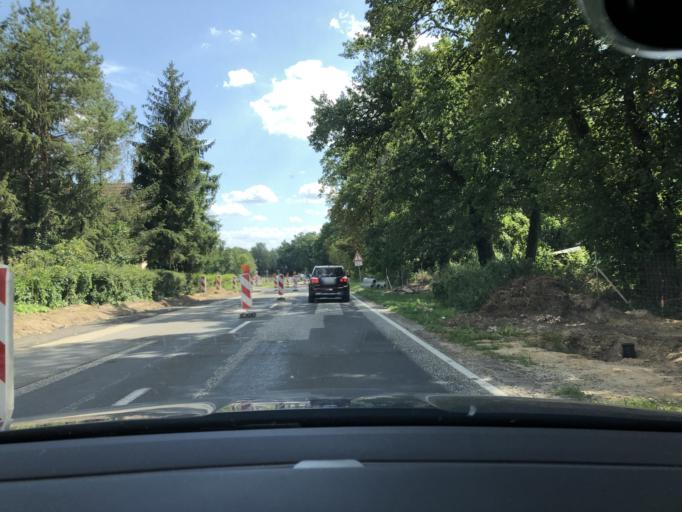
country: DE
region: Brandenburg
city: Neuruppin
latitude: 52.9280
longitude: 12.8977
